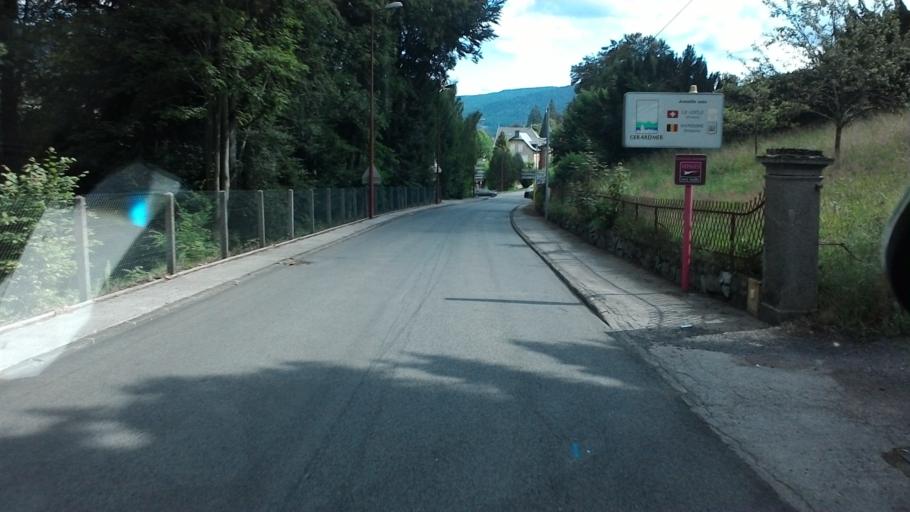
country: FR
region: Lorraine
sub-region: Departement des Vosges
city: Gerardmer
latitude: 48.0646
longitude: 6.8642
